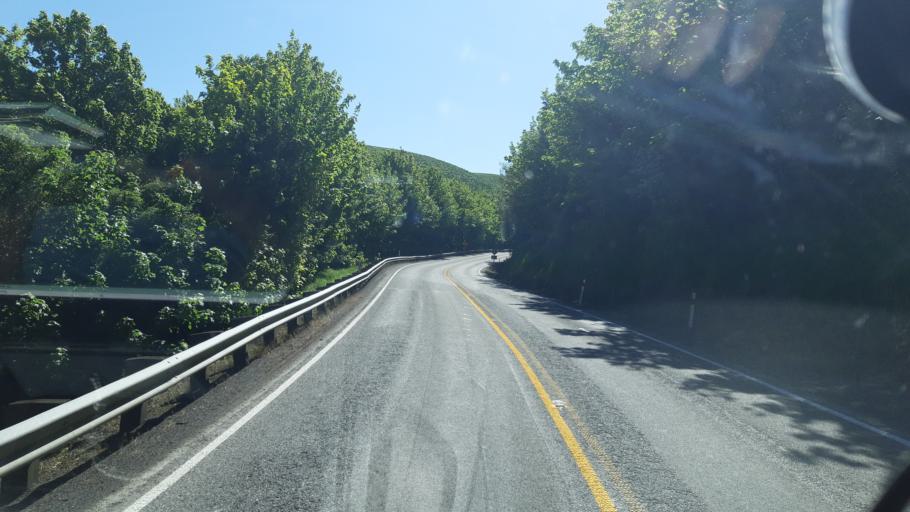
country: NZ
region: Otago
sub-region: Clutha District
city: Milton
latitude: -46.0781
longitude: 169.8457
